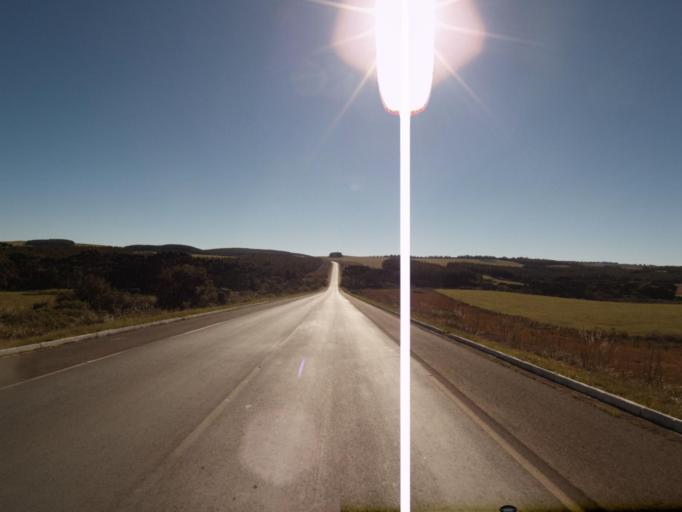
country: BR
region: Parana
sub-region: Palmas
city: Palmas
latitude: -26.7621
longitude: -51.6677
